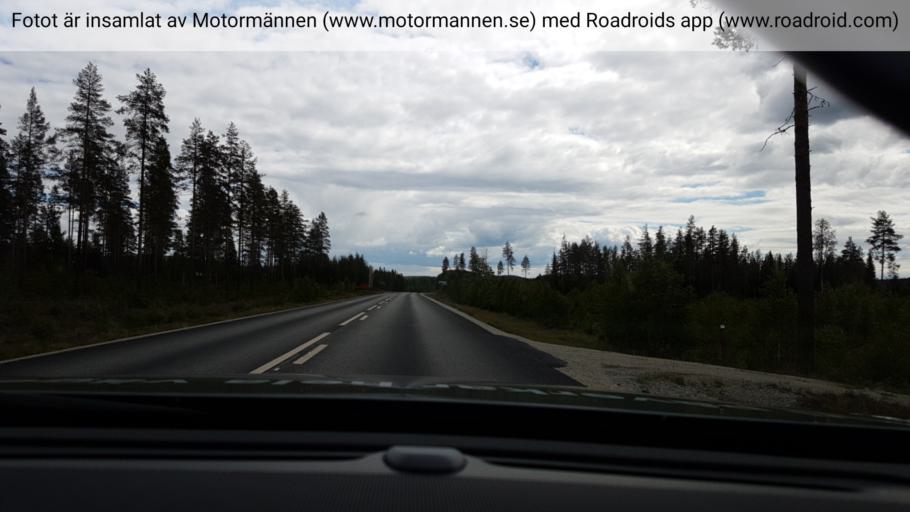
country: SE
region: Vaesterbotten
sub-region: Vindelns Kommun
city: Vindeln
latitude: 64.0602
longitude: 19.6440
